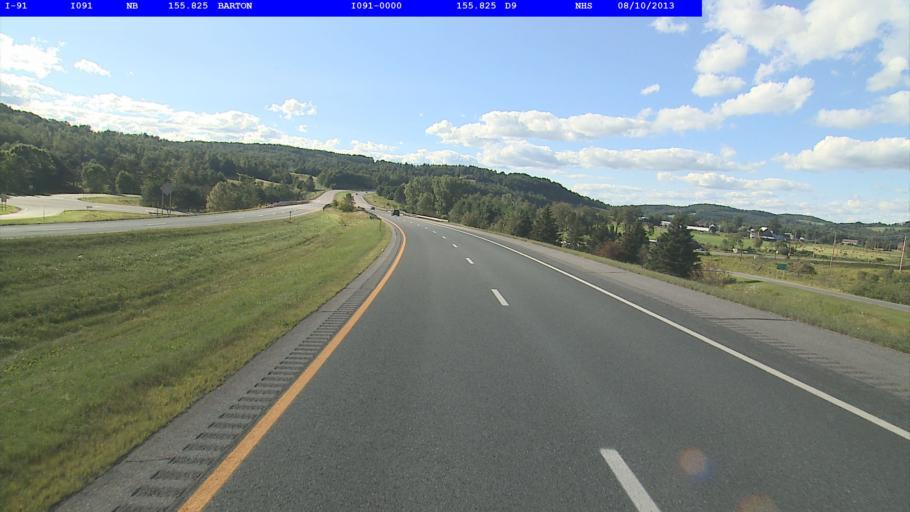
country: US
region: Vermont
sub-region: Orleans County
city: Newport
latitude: 44.7342
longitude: -72.1816
